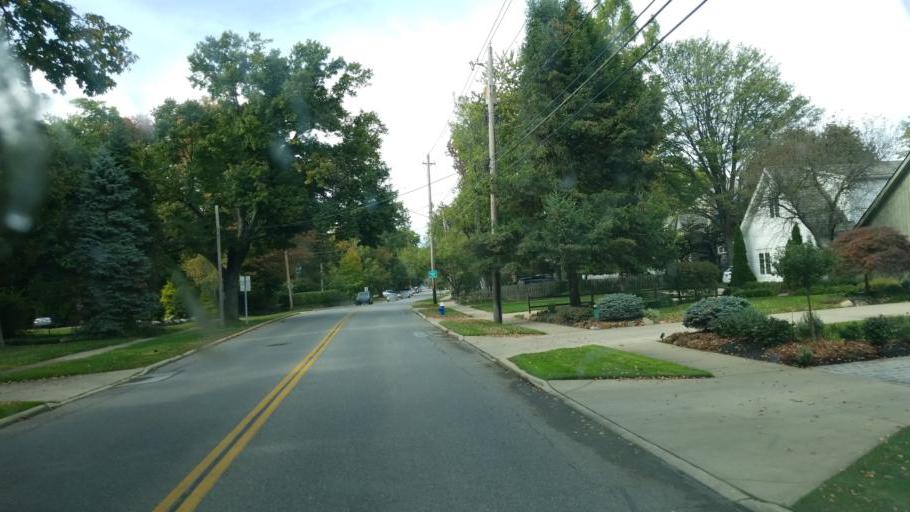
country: US
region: Ohio
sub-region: Cuyahoga County
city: Bay Village
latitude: 41.4967
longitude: -81.9573
